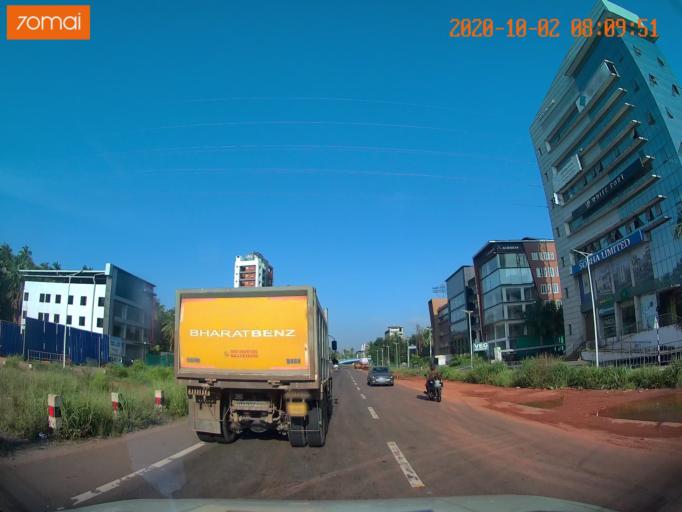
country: IN
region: Kerala
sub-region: Kozhikode
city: Kozhikode
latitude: 11.2632
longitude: 75.8166
